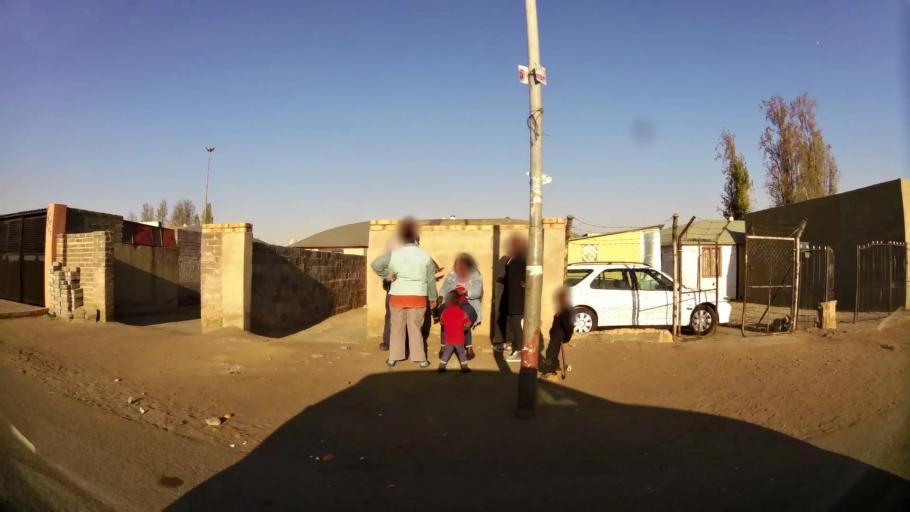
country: ZA
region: Gauteng
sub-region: City of Johannesburg Metropolitan Municipality
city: Soweto
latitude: -26.2551
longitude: 27.8806
